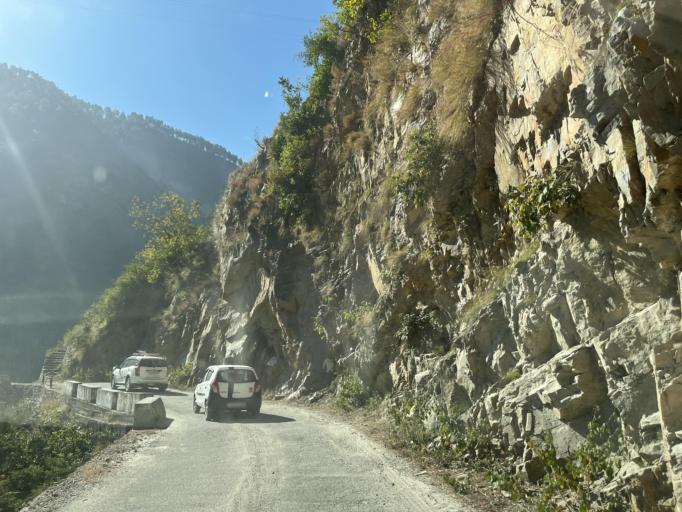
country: IN
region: Uttarakhand
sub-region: Naini Tal
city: Naini Tal
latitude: 29.5098
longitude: 79.4655
